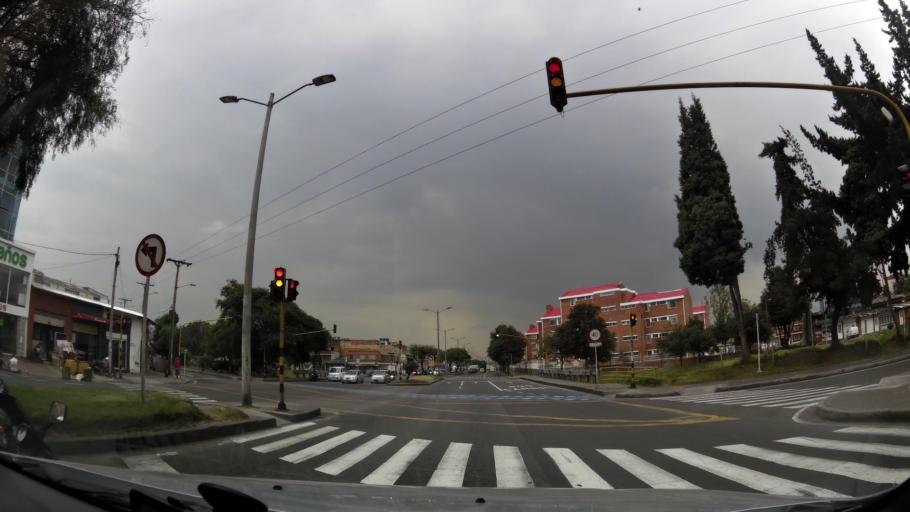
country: CO
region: Bogota D.C.
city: Bogota
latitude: 4.6060
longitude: -74.1194
